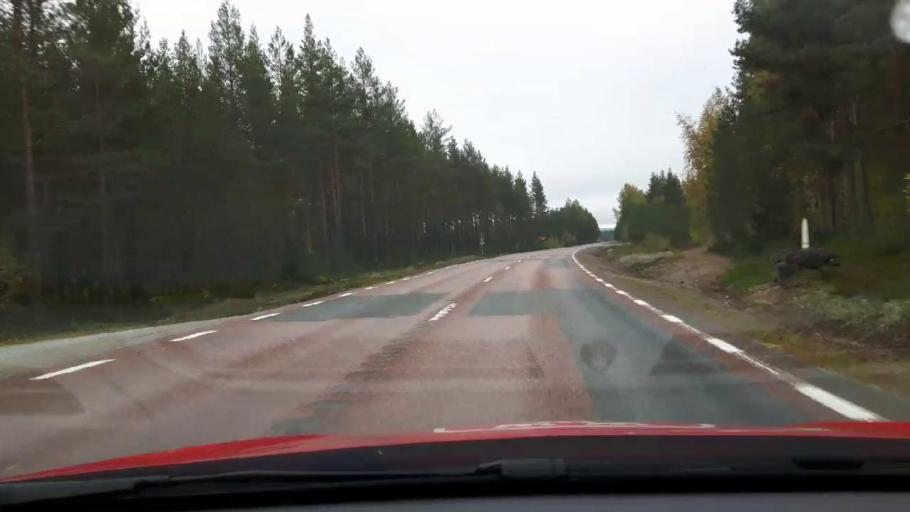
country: SE
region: Gaevleborg
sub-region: Ljusdals Kommun
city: Farila
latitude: 61.8489
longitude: 15.7517
